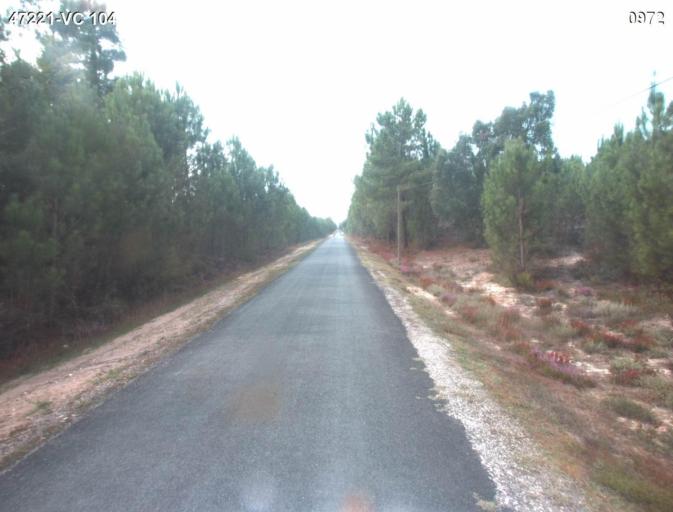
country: FR
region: Aquitaine
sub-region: Departement du Lot-et-Garonne
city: Mezin
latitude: 44.1242
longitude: 0.2163
